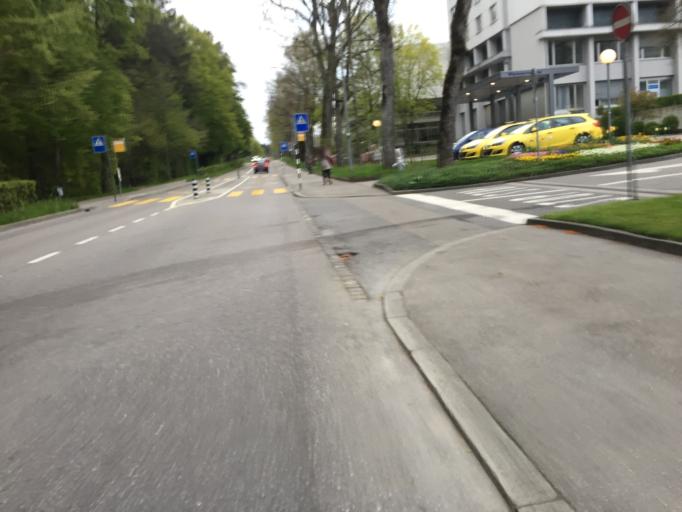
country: CH
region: Bern
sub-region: Bern-Mittelland District
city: Bern
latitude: 46.9588
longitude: 7.4269
